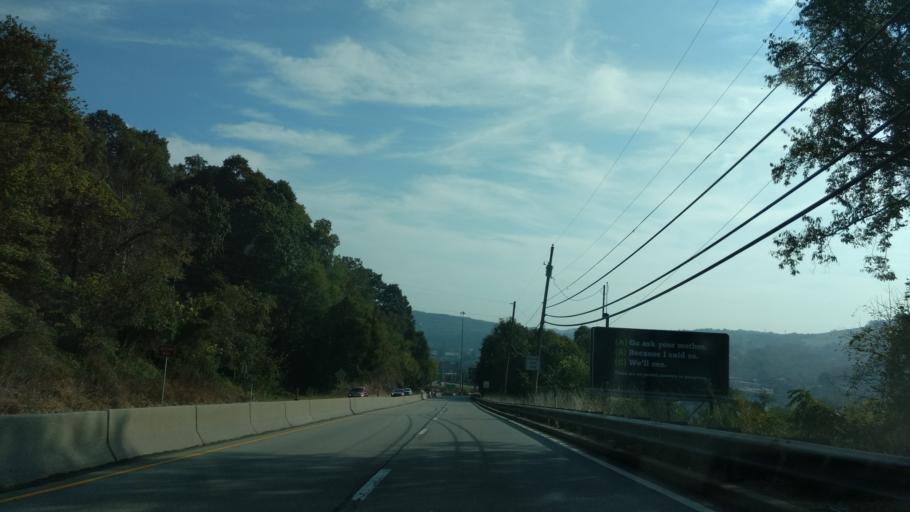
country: US
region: Pennsylvania
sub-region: Allegheny County
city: Elizabeth
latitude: 40.2737
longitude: -79.8982
